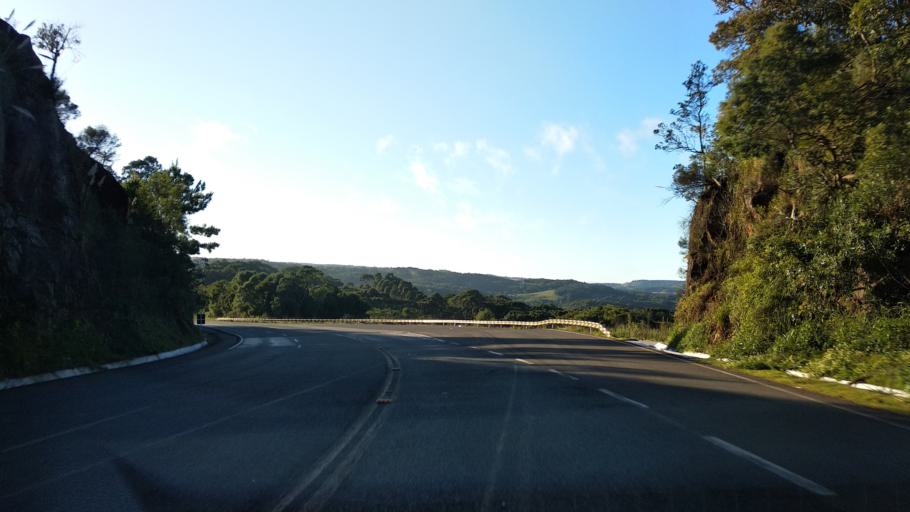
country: BR
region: Santa Catarina
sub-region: Correia Pinto
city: Correia Pinto
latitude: -27.6250
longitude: -50.6558
